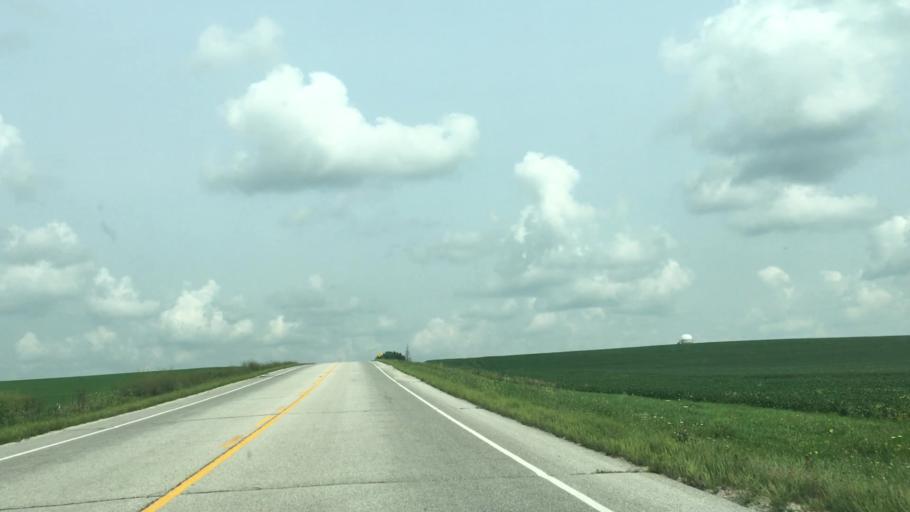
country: US
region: Minnesota
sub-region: Fillmore County
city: Harmony
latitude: 43.5978
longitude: -91.9297
